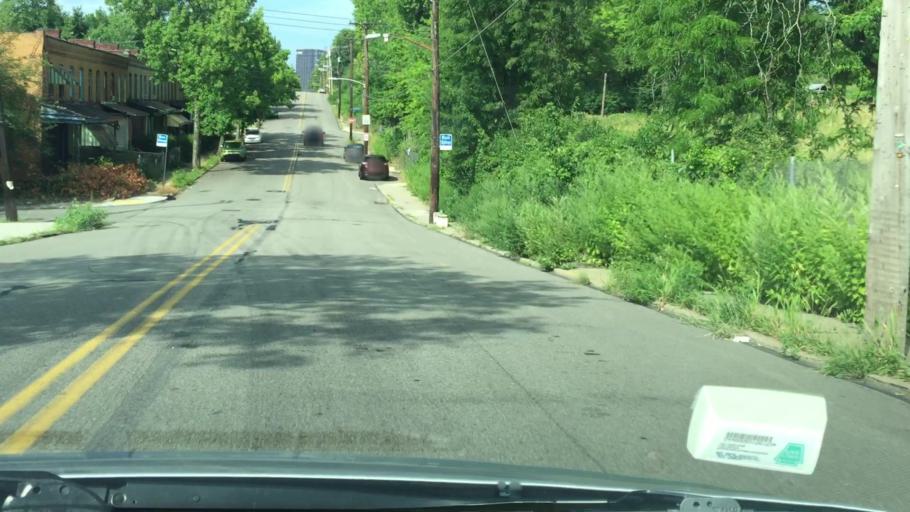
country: US
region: Pennsylvania
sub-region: Allegheny County
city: Bloomfield
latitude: 40.4521
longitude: -79.9691
